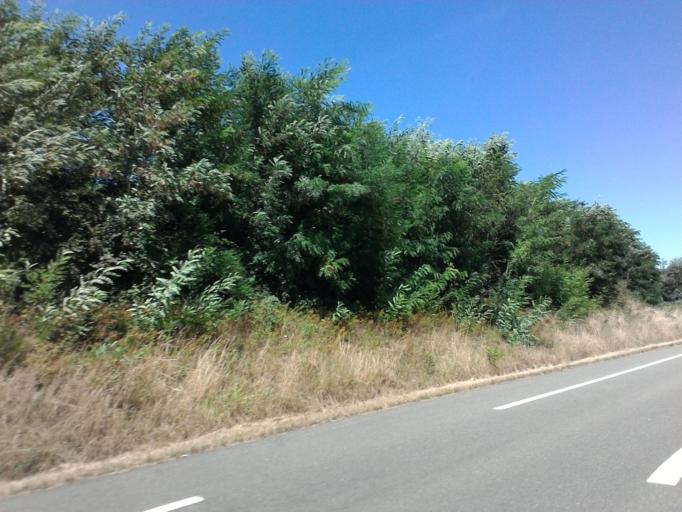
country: FR
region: Franche-Comte
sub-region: Departement du Jura
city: Montmorot
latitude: 46.6694
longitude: 5.5078
